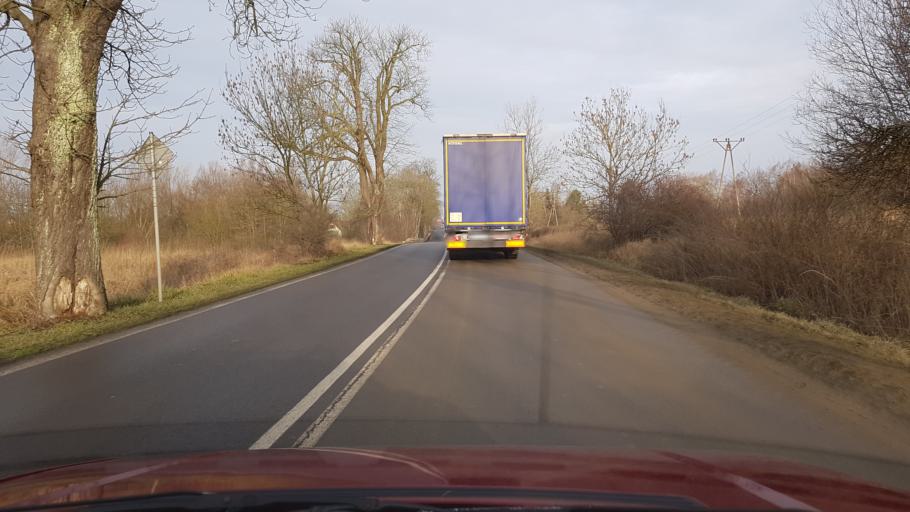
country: PL
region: West Pomeranian Voivodeship
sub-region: Powiat policki
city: Police
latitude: 53.4962
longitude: 14.5830
